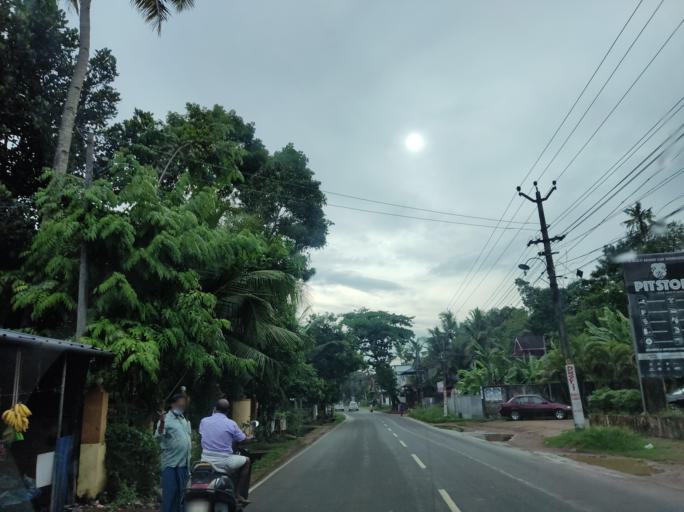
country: IN
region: Kerala
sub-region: Pattanamtitta
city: Adur
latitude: 9.1625
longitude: 76.7103
